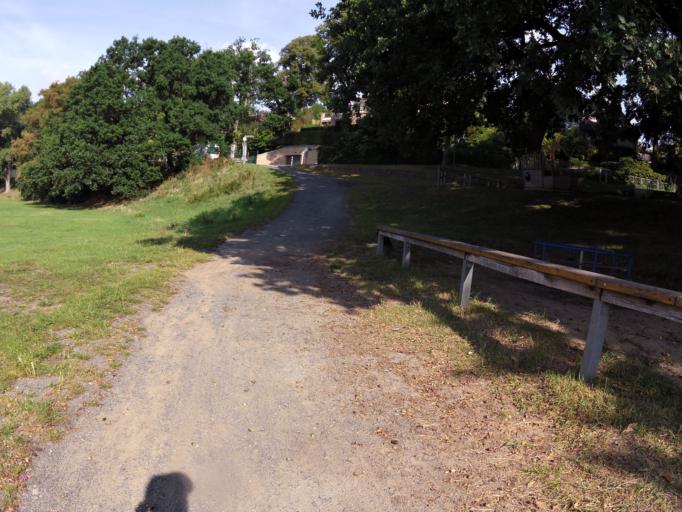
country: DE
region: Lower Saxony
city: Ahsen-Oetzen
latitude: 52.9966
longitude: 9.0789
